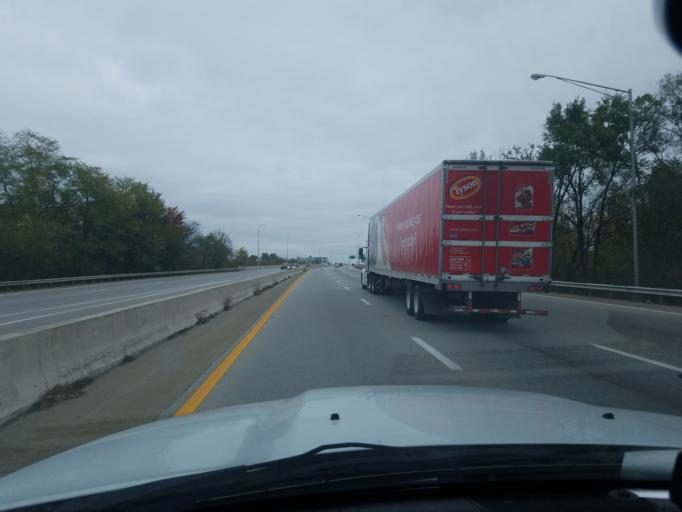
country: US
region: Indiana
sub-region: Floyd County
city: New Albany
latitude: 38.2772
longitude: -85.8048
